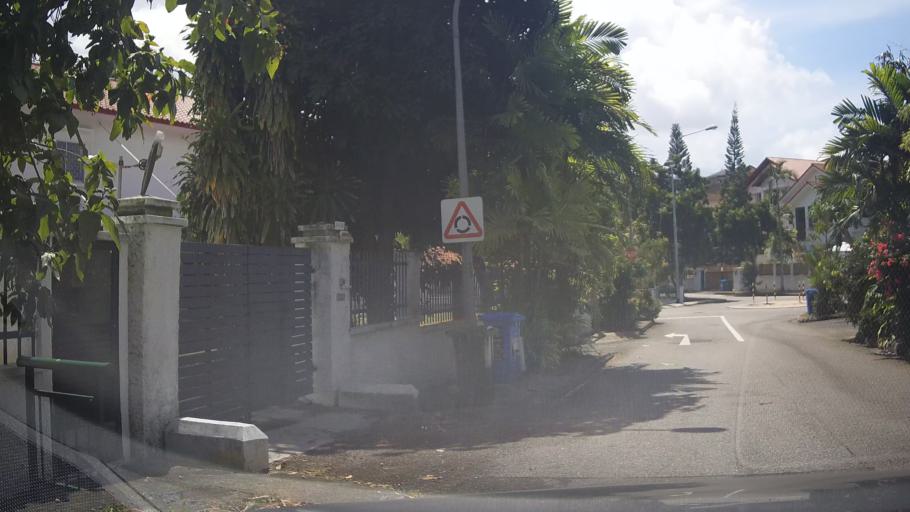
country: MY
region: Johor
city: Kampung Pasir Gudang Baru
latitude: 1.3653
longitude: 103.9712
